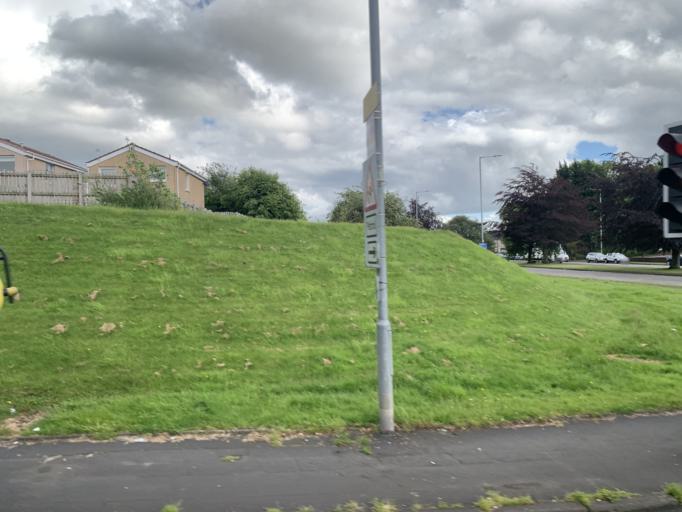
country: GB
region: Scotland
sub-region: South Lanarkshire
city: Uddingston
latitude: 55.8545
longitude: -4.1110
